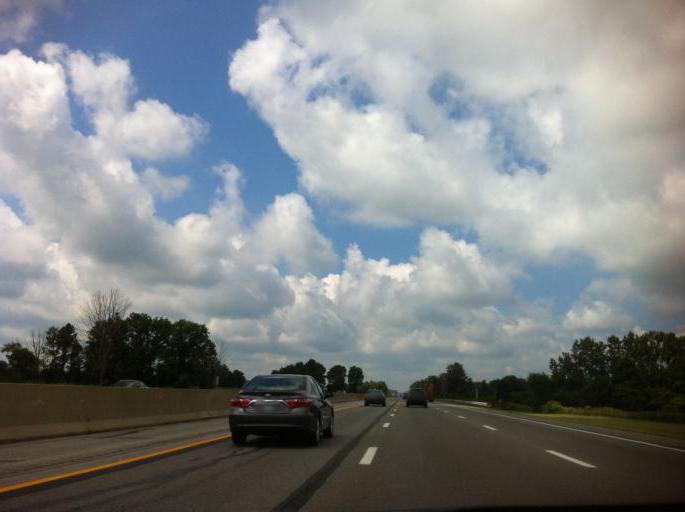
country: US
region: Ohio
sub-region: Huron County
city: Wakeman
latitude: 41.3326
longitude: -82.4266
